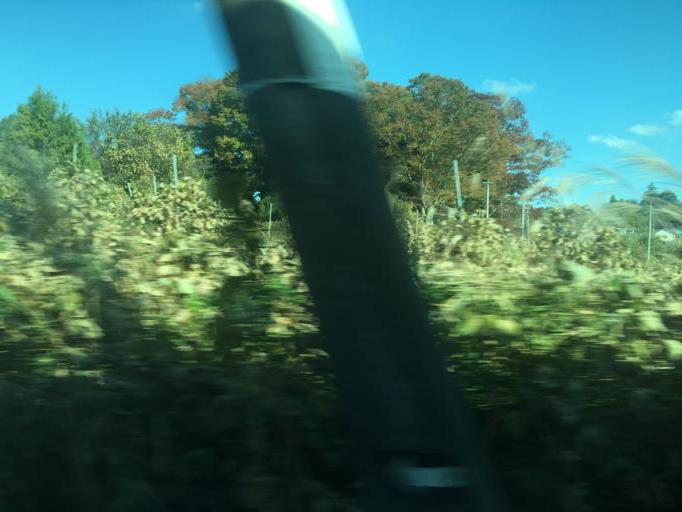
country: JP
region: Ibaraki
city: Kasama
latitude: 36.3695
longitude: 140.2543
